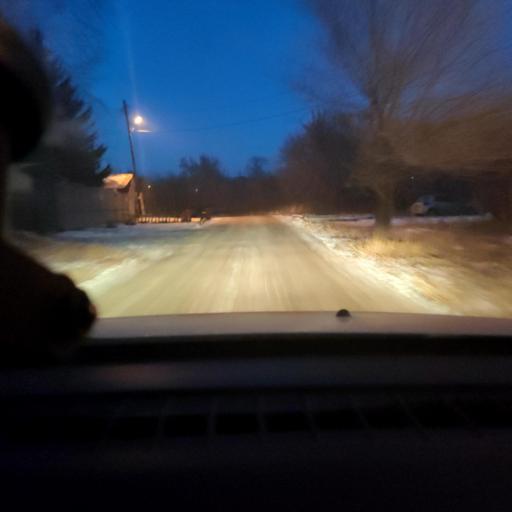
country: RU
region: Samara
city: Petra-Dubrava
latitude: 53.2570
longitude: 50.3390
